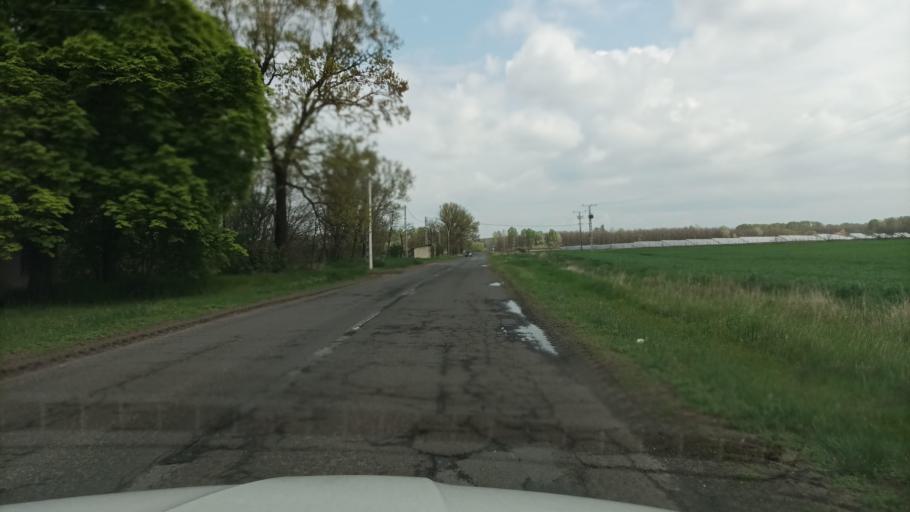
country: HU
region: Pest
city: Nagykoros
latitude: 47.0510
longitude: 19.8416
